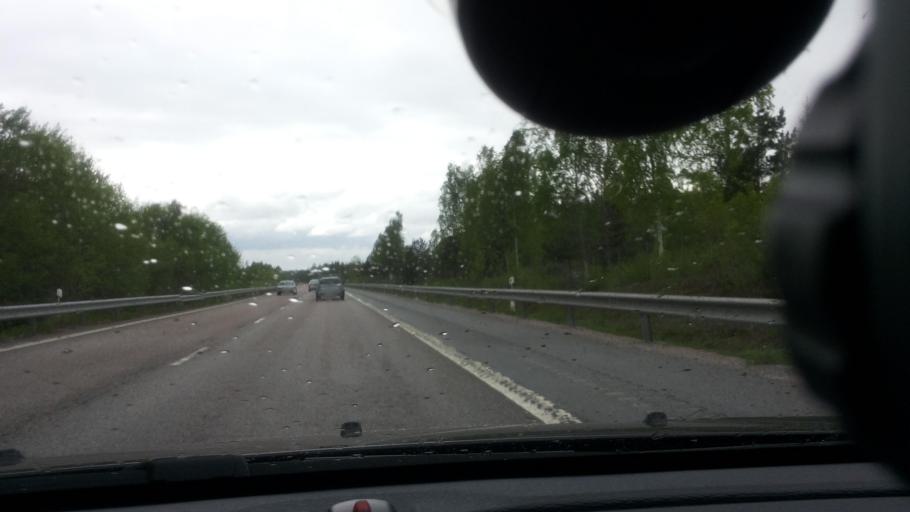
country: SE
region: Uppsala
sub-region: Alvkarleby Kommun
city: AElvkarleby
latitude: 60.4848
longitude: 17.3583
